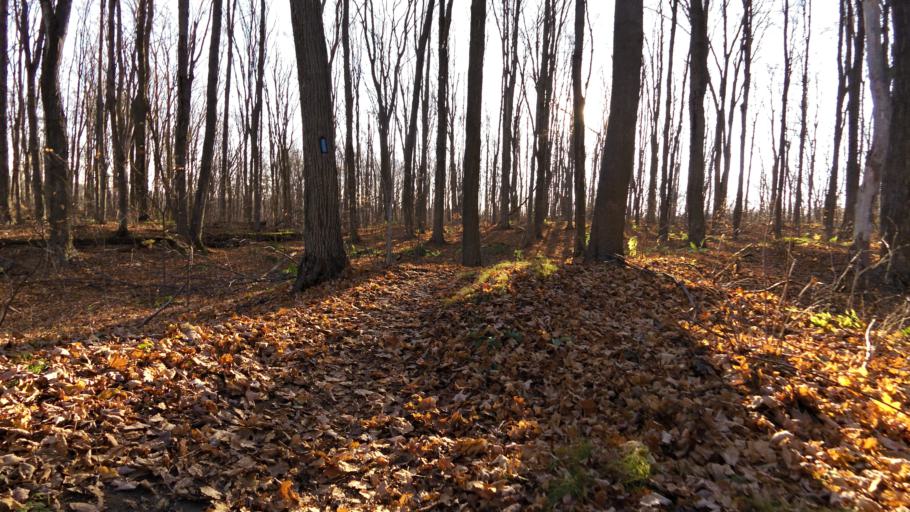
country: CA
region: Ontario
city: Orangeville
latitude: 43.9936
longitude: -80.0568
